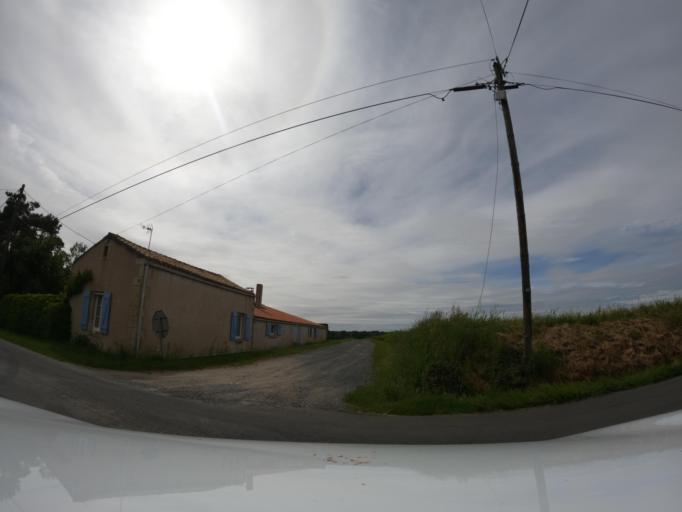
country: FR
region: Pays de la Loire
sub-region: Departement de la Vendee
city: Saint-Hilaire-des-Loges
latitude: 46.5042
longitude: -0.6484
